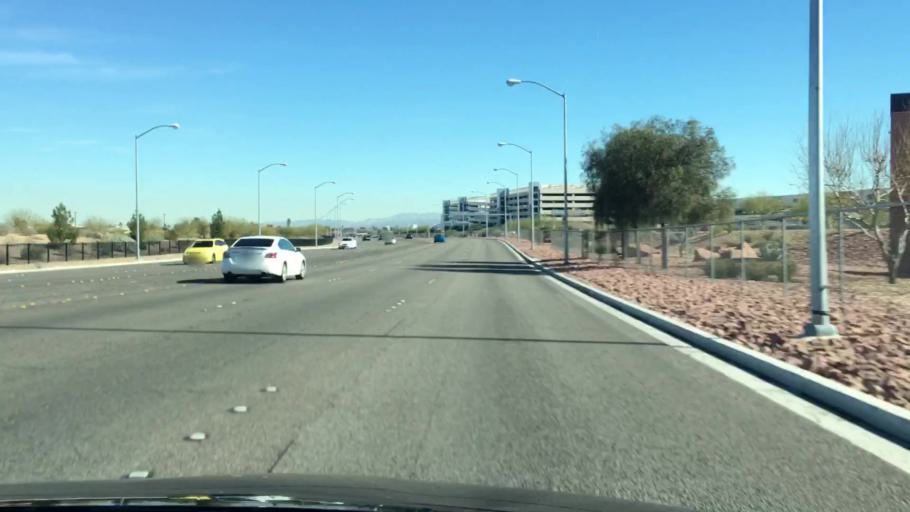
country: US
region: Nevada
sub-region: Clark County
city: Paradise
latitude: 36.0891
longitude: -115.1436
